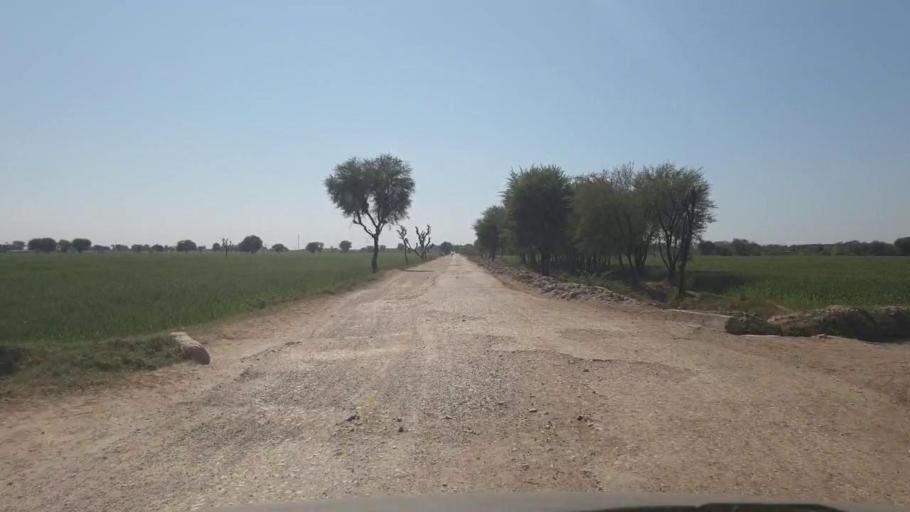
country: PK
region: Sindh
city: Dhoro Naro
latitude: 25.4750
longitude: 69.6094
